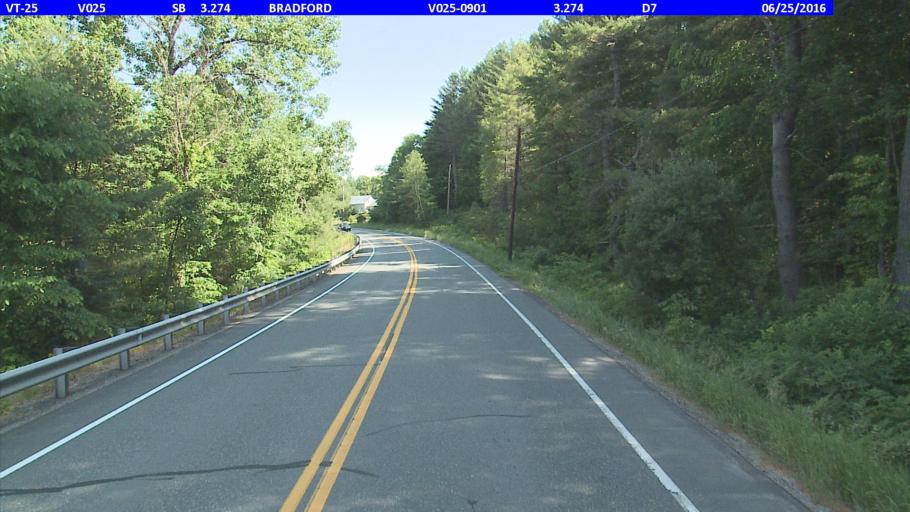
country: US
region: New Hampshire
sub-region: Grafton County
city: Orford
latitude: 44.0018
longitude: -72.1619
